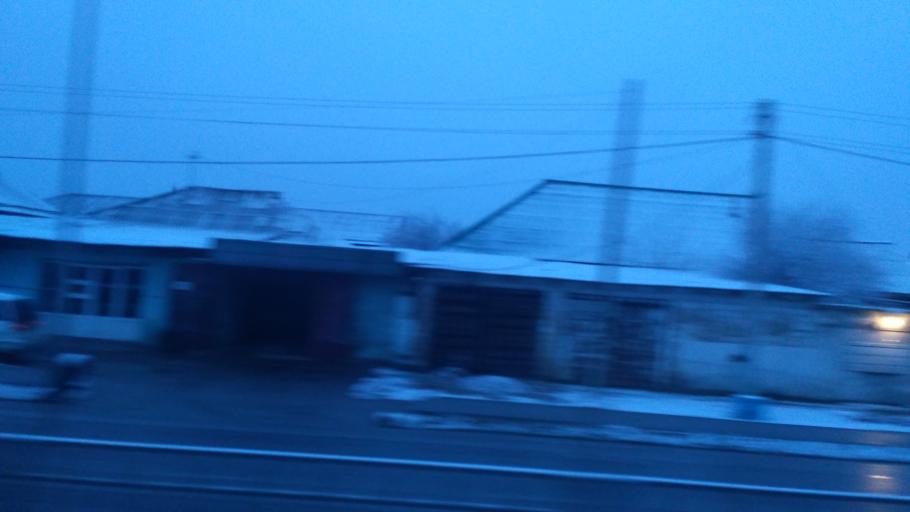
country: KZ
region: Ongtustik Qazaqstan
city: Shymkent
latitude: 42.3757
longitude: 69.5000
